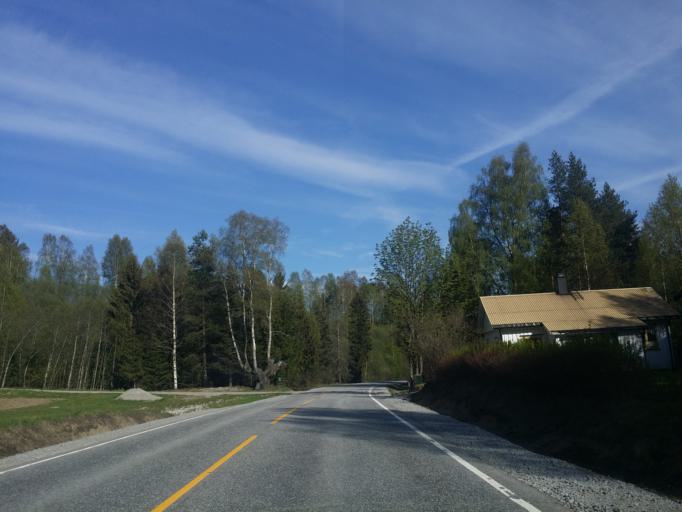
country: NO
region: Telemark
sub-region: Hjartdal
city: Sauland
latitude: 59.6232
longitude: 8.9073
